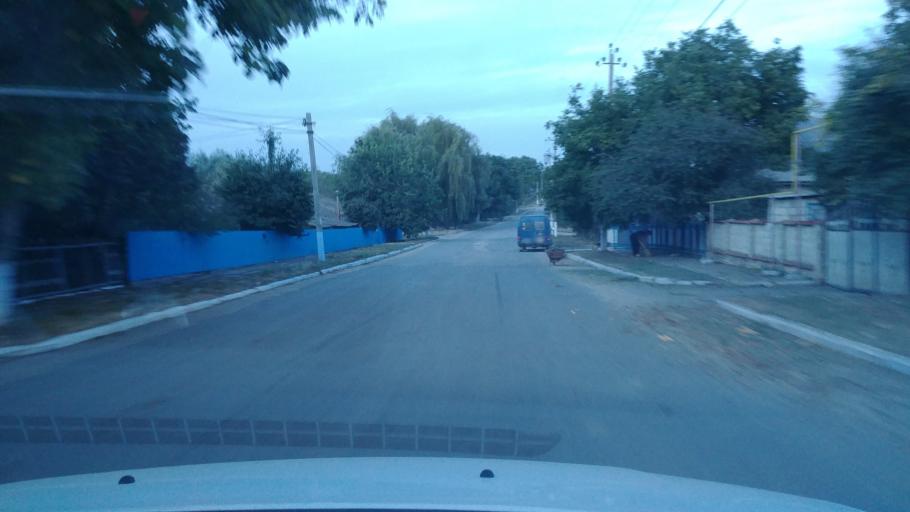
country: MD
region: Rezina
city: Saharna
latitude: 47.6752
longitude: 28.9589
